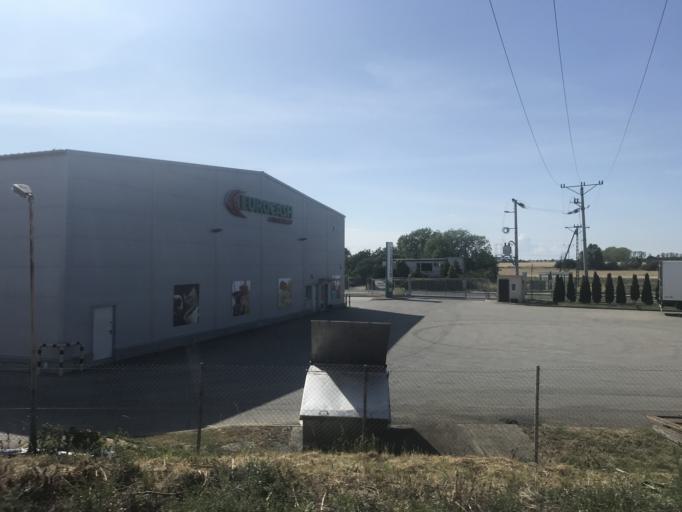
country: PL
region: West Pomeranian Voivodeship
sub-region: Powiat policki
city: Przeclaw
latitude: 53.3863
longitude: 14.4705
